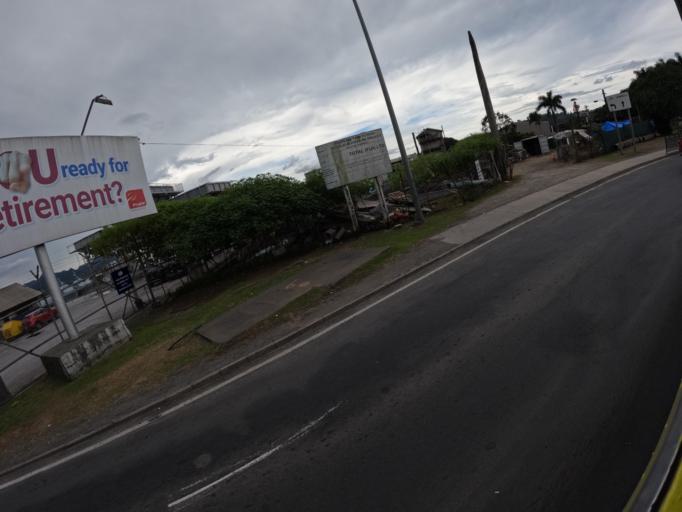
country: FJ
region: Central
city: Suva
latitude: -18.1322
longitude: 178.4264
